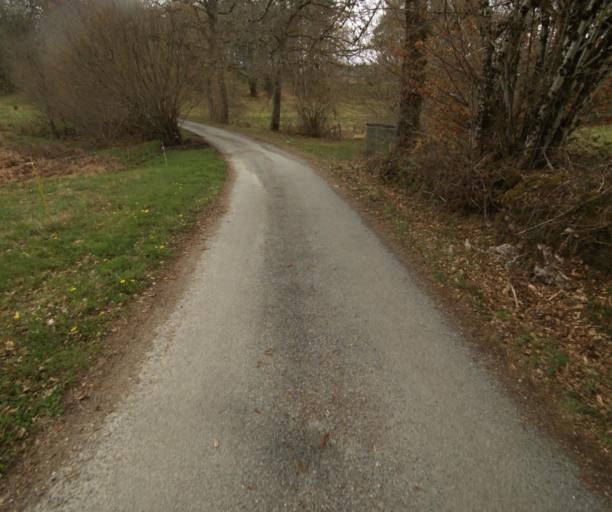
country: FR
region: Limousin
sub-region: Departement de la Correze
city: Correze
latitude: 45.3384
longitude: 1.9450
